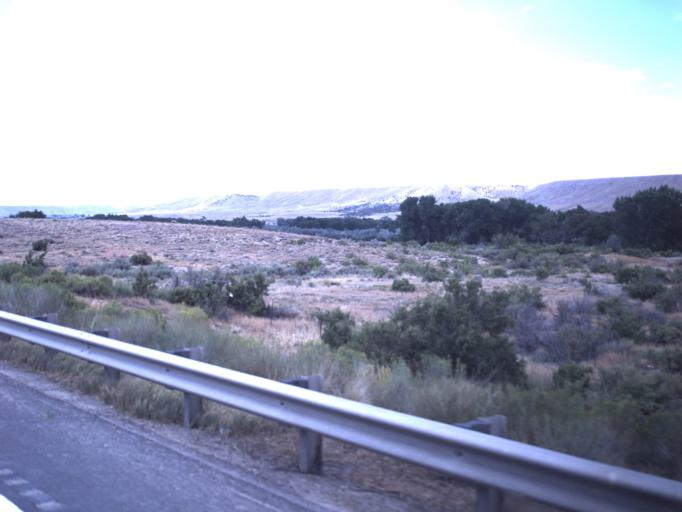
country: US
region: Utah
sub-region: Duchesne County
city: Duchesne
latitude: 40.1537
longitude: -110.2427
